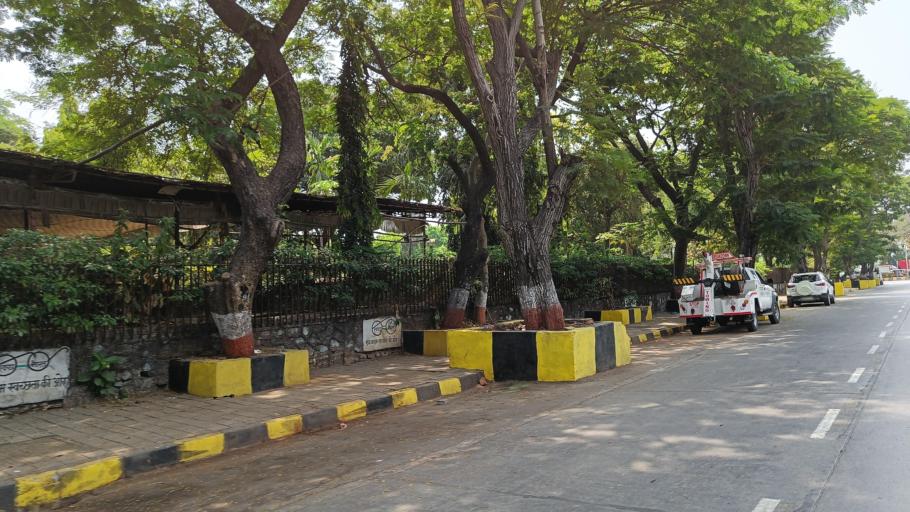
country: IN
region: Maharashtra
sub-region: Mumbai Suburban
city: Mumbai
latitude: 19.1053
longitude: 72.8299
